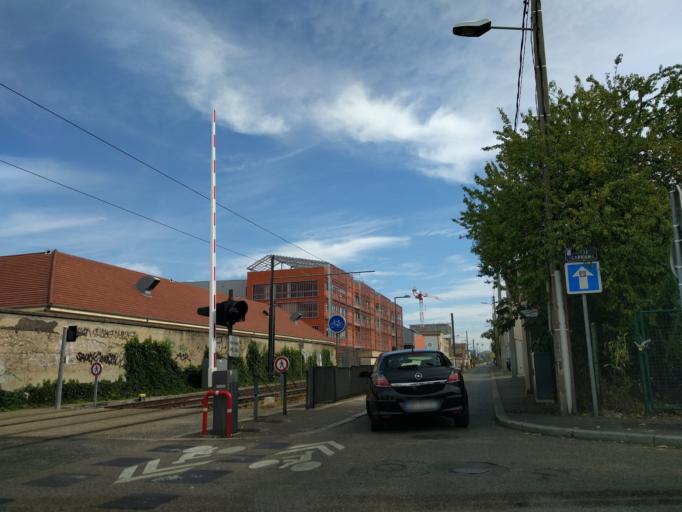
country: FR
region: Rhone-Alpes
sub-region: Departement du Rhone
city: Villeurbanne
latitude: 45.7570
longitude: 4.9021
